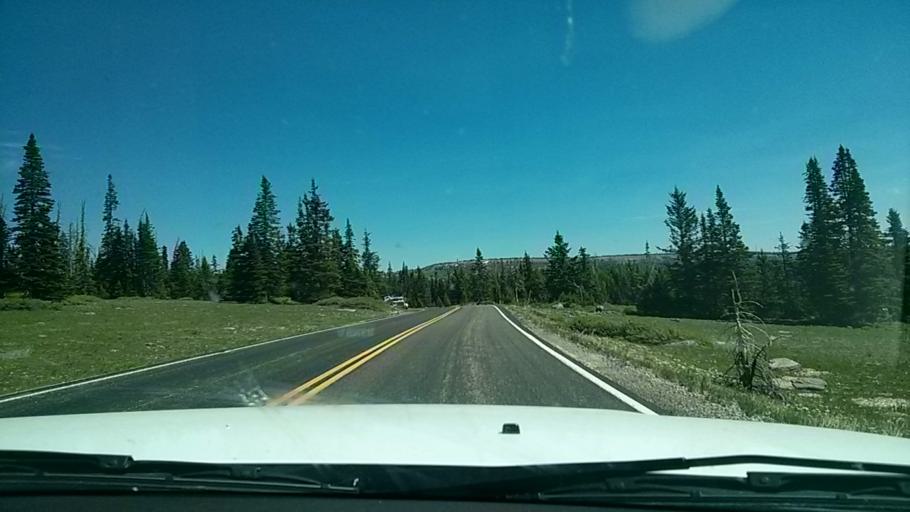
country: US
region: Utah
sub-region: Iron County
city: Parowan
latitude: 37.6382
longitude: -112.8219
